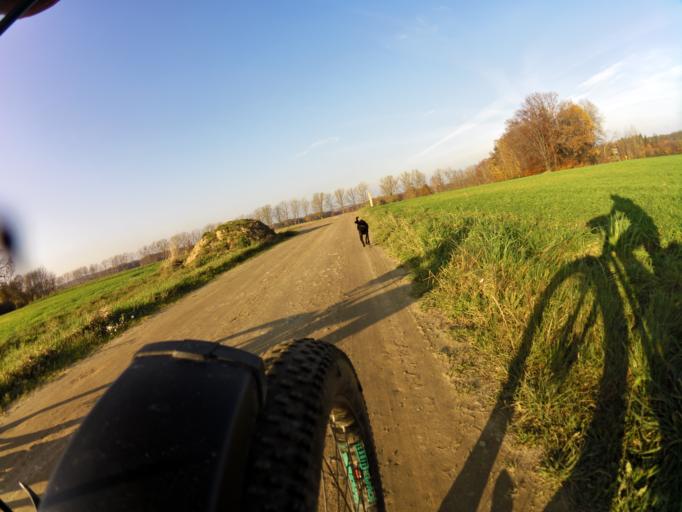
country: PL
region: Pomeranian Voivodeship
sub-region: Powiat pucki
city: Krokowa
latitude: 54.7328
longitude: 18.1973
